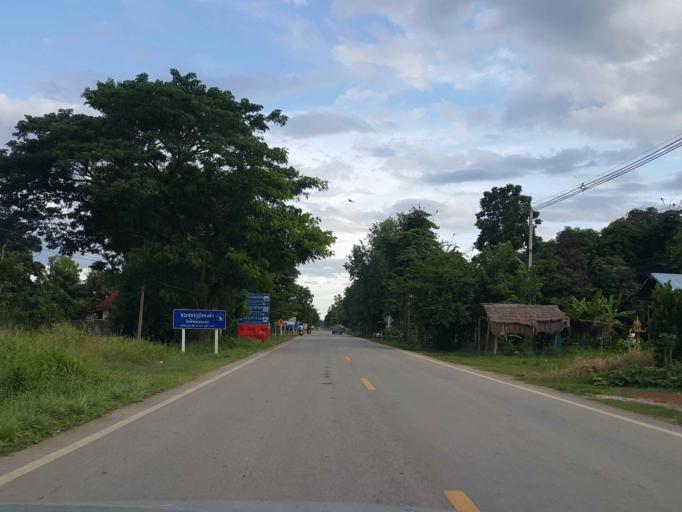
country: TH
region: Sukhothai
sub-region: Amphoe Si Satchanalai
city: Si Satchanalai
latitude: 17.5005
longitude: 99.7524
